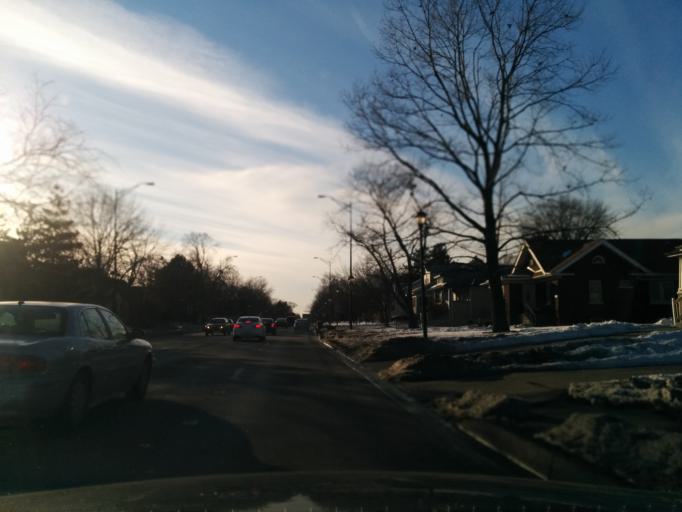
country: US
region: Illinois
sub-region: DuPage County
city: Elmhurst
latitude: 41.9065
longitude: -87.9319
